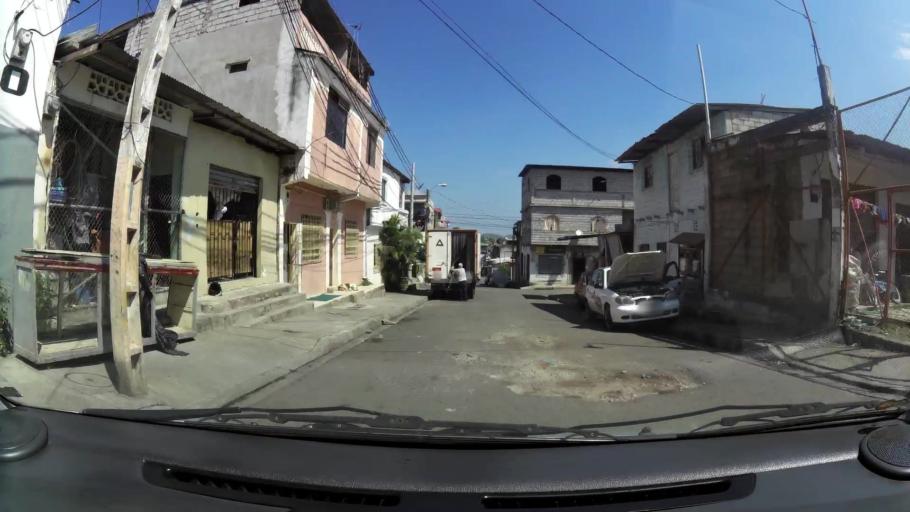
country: EC
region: Guayas
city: Guayaquil
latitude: -2.1312
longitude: -79.9203
